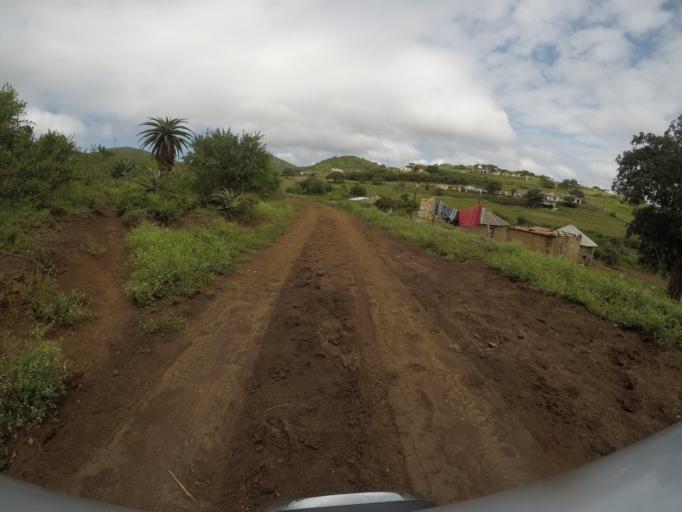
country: ZA
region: KwaZulu-Natal
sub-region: uThungulu District Municipality
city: Empangeni
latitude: -28.6261
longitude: 31.8727
